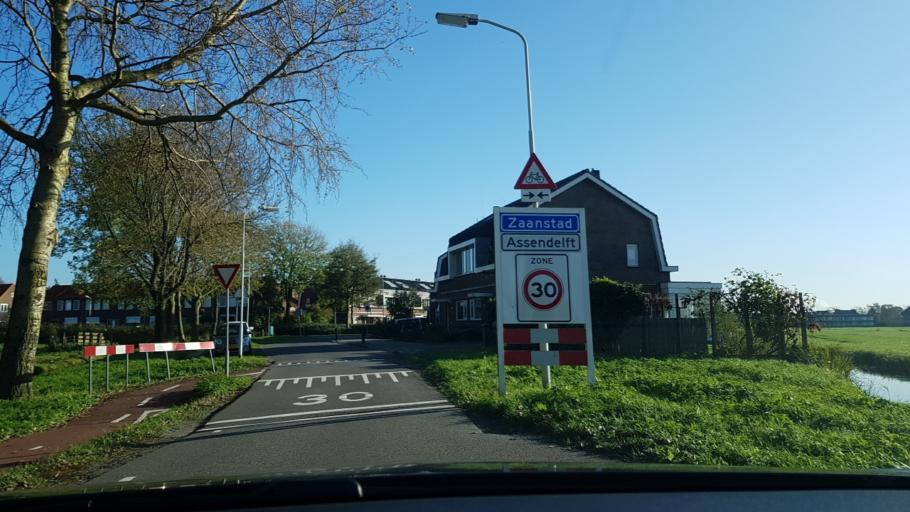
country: NL
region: North Holland
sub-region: Gemeente Uitgeest
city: Uitgeest
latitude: 52.4657
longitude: 4.7336
